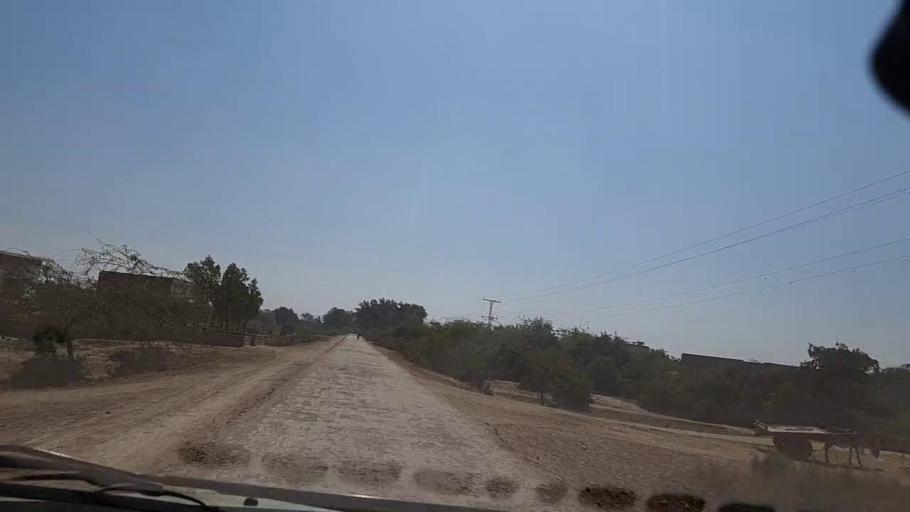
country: PK
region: Sindh
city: Mirpur Khas
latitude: 25.4767
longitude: 69.0486
